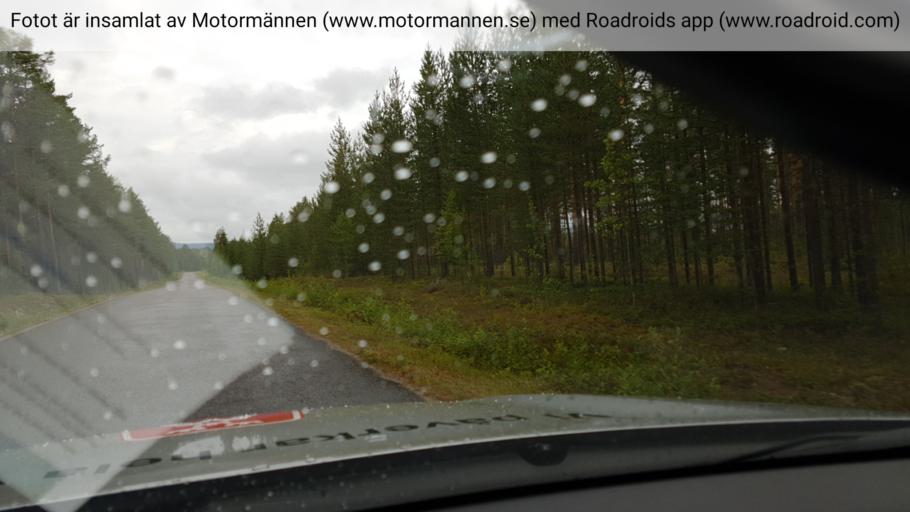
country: SE
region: Norrbotten
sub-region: Alvsbyns Kommun
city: AElvsbyn
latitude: 66.0721
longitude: 20.9298
